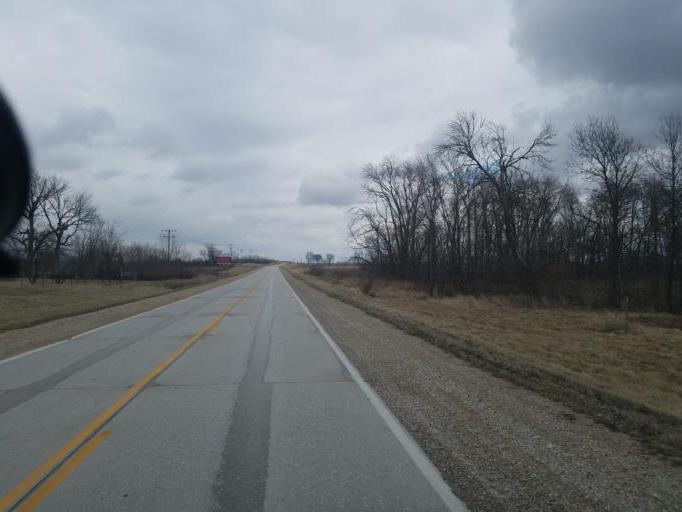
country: US
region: Missouri
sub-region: Boone County
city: Hallsville
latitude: 39.2464
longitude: -92.3172
